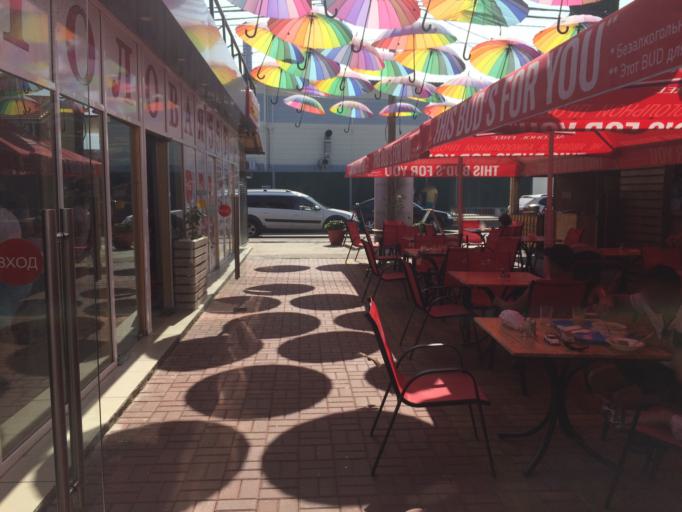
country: RU
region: Krasnodarskiy
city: Adler
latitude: 43.3978
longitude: 39.9680
